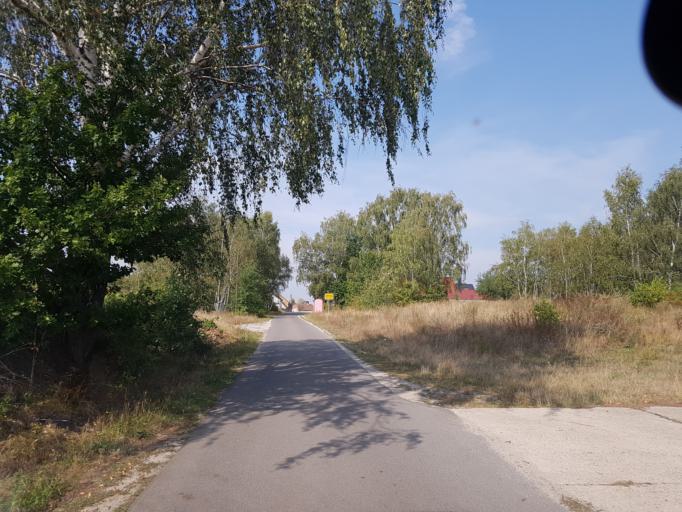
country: DE
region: Brandenburg
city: Finsterwalde
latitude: 51.6642
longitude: 13.7412
